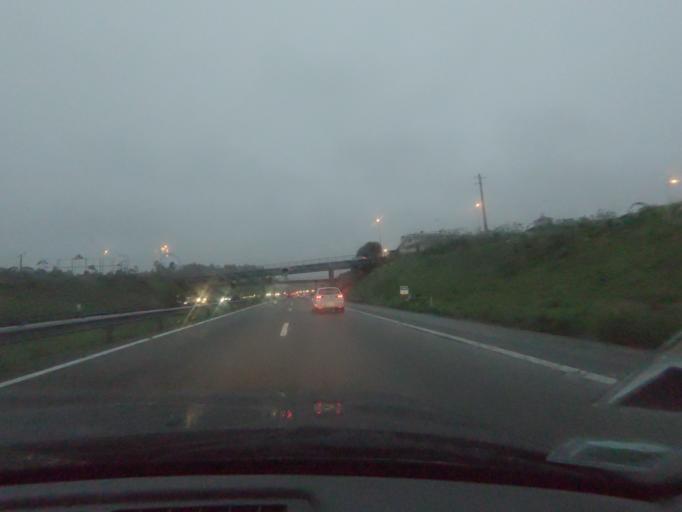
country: PT
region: Porto
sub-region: Matosinhos
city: Lavra
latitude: 41.2510
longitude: -8.6980
